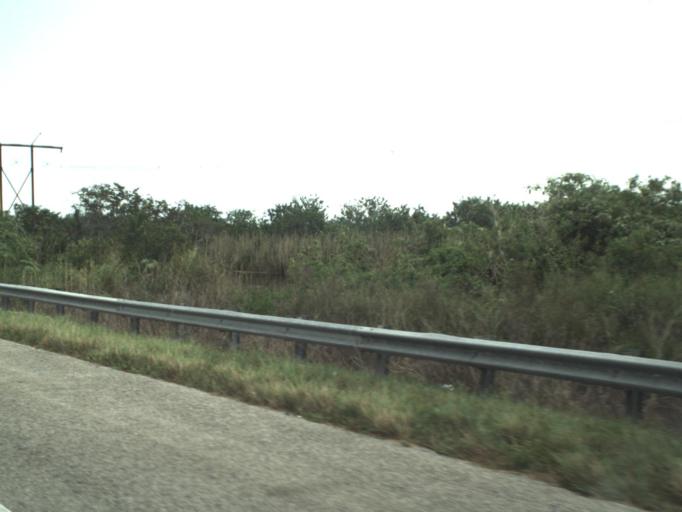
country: US
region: Florida
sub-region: Broward County
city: Weston
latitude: 26.3053
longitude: -80.5148
